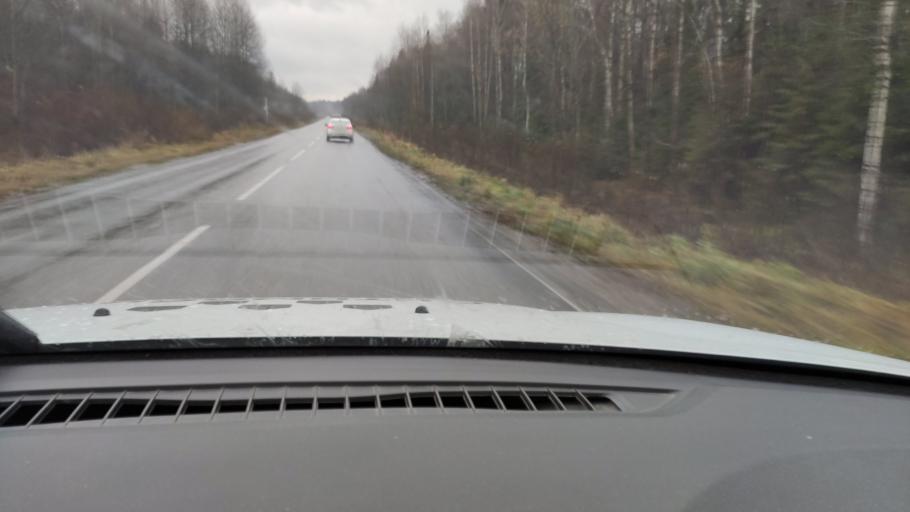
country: RU
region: Perm
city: Novyye Lyady
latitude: 58.0259
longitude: 56.6324
